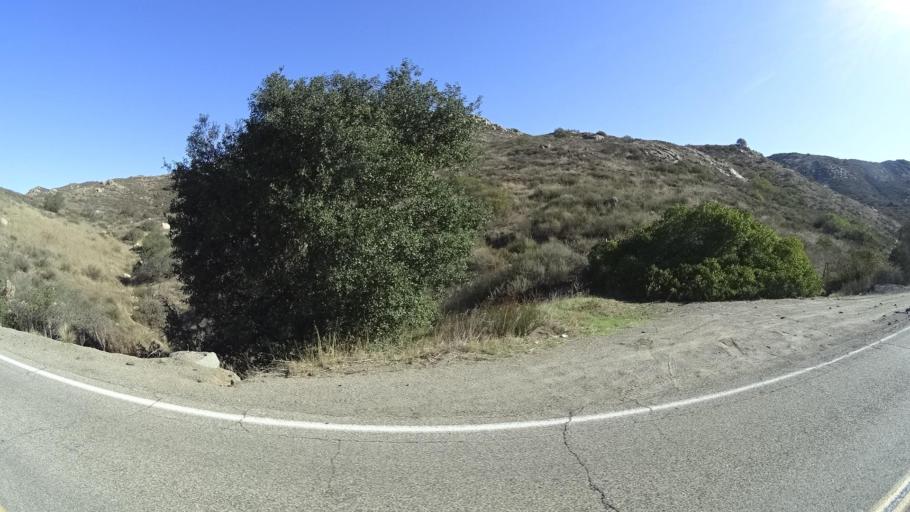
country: US
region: California
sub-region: San Diego County
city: Jamul
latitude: 32.6721
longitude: -116.8047
